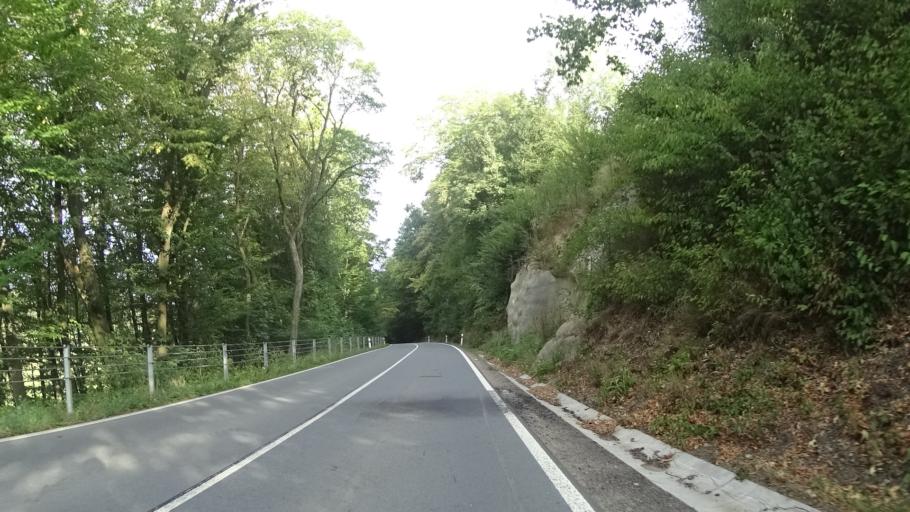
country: CZ
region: Pardubicky
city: Kuncina
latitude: 49.8611
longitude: 16.7093
